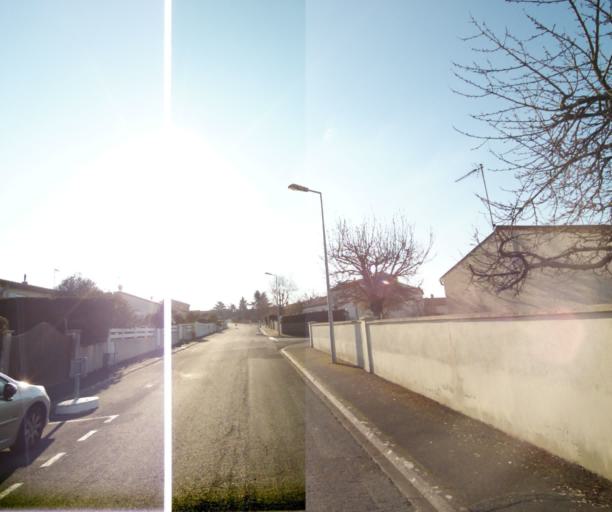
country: FR
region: Poitou-Charentes
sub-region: Departement des Deux-Sevres
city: Niort
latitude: 46.3441
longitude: -0.4484
